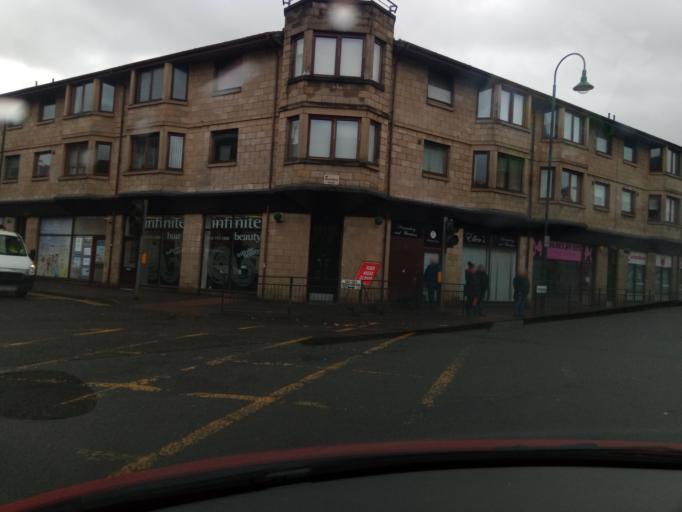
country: GB
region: Scotland
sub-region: East Dunbartonshire
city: Kirkintilloch
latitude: 55.9358
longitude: -4.1522
